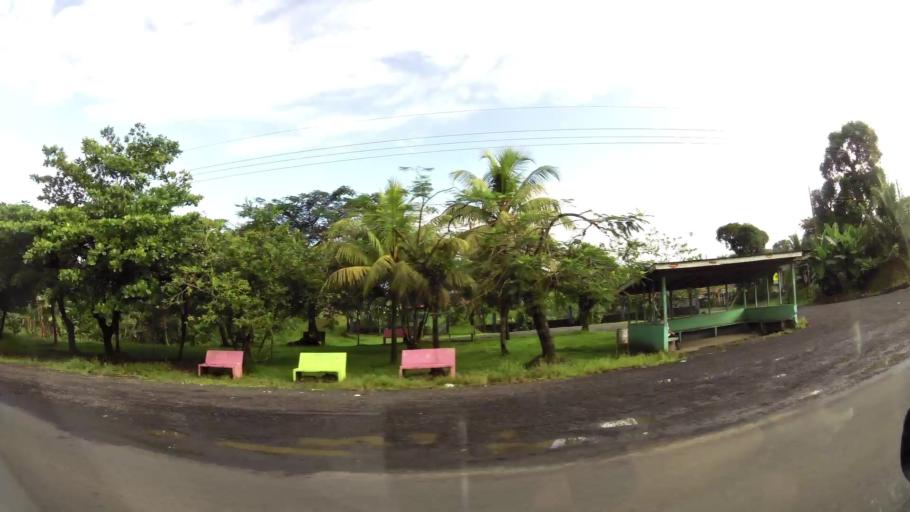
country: CR
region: Limon
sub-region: Canton de Guacimo
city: Guacimo
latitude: 10.1962
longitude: -83.6492
